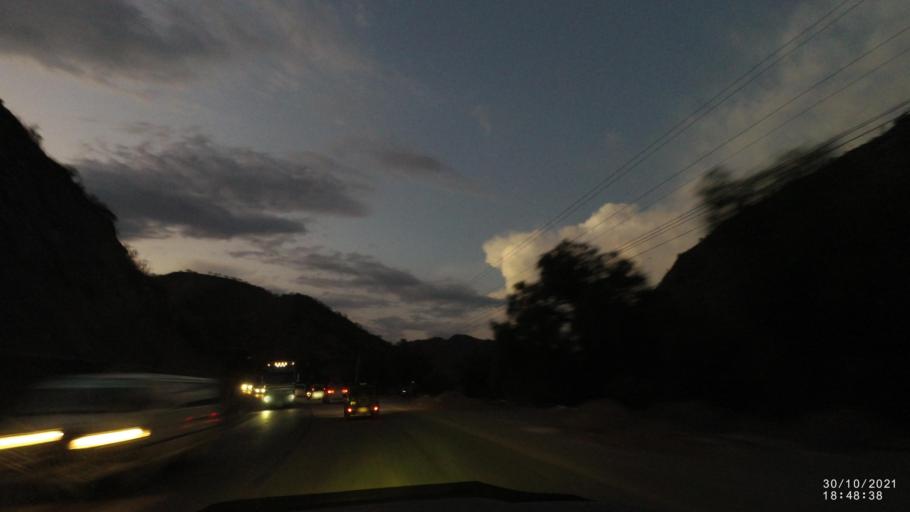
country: BO
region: Cochabamba
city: Sipe Sipe
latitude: -17.5147
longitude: -66.3335
